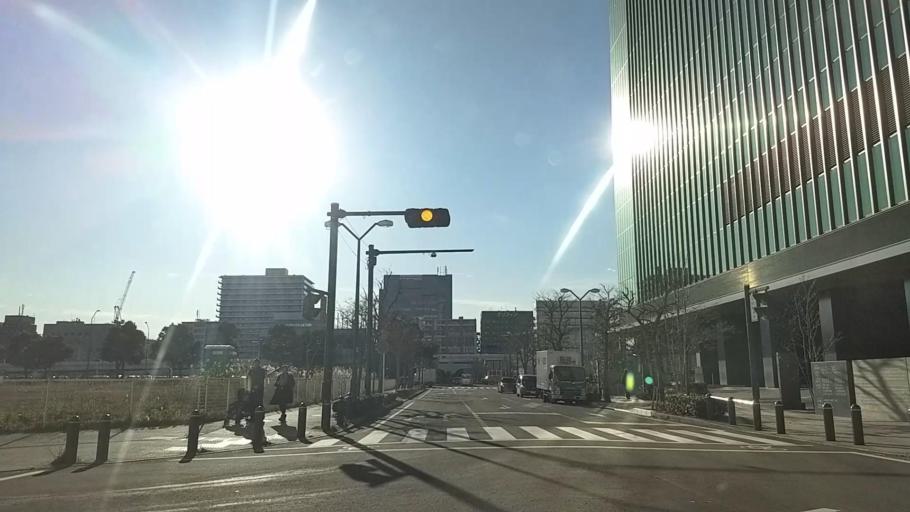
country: JP
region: Kanagawa
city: Yokohama
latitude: 35.4594
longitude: 139.6282
